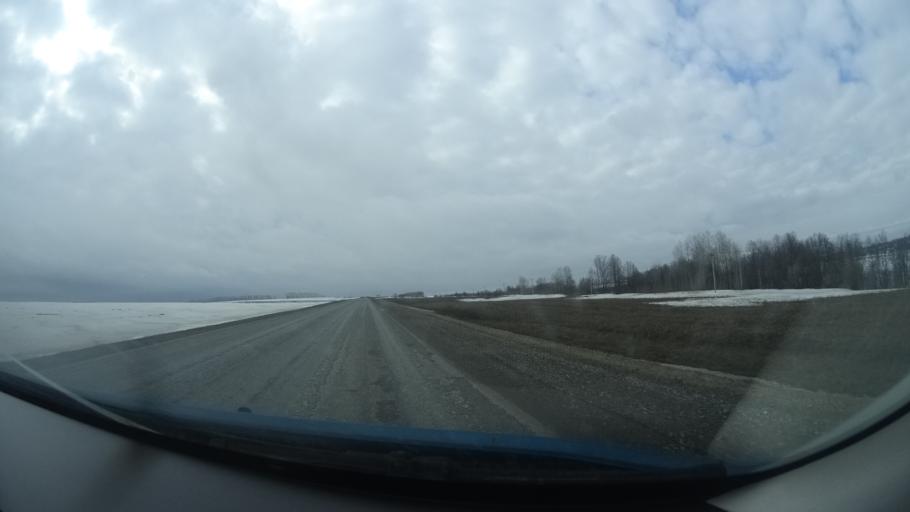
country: RU
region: Bashkortostan
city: Birsk
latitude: 55.4009
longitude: 55.5873
